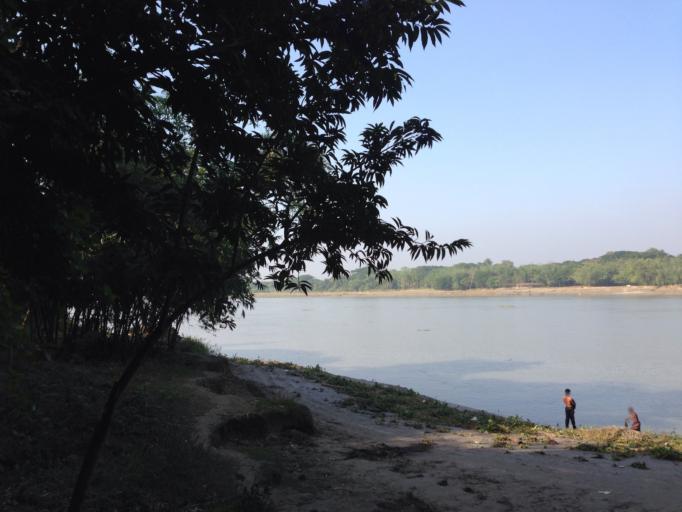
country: BD
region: Khulna
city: Kalia
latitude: 23.0564
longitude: 89.6449
